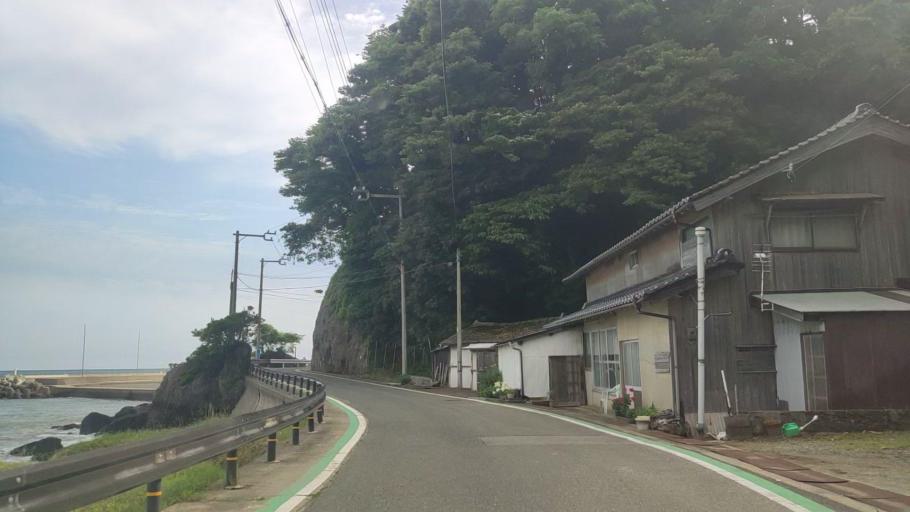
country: JP
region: Hyogo
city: Toyooka
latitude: 35.6427
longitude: 134.8427
